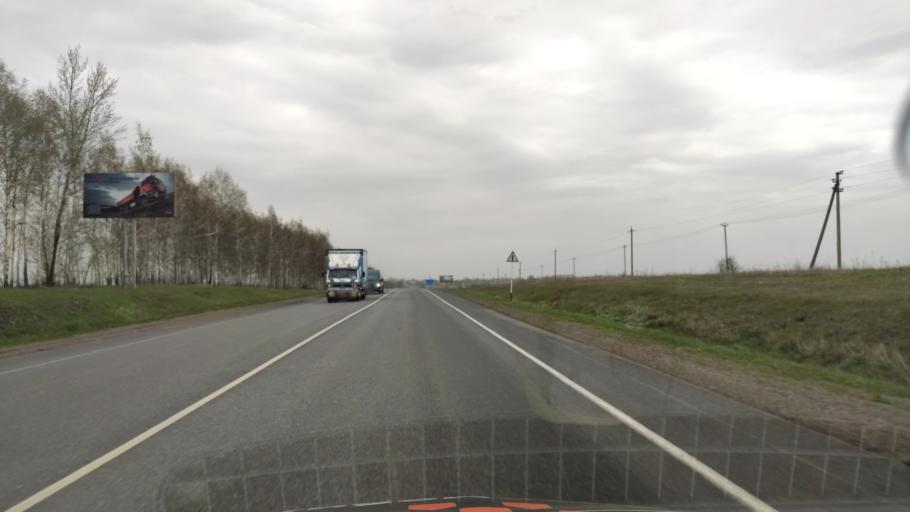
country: RU
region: Kursk
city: Gorshechnoye
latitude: 51.5041
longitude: 37.9905
